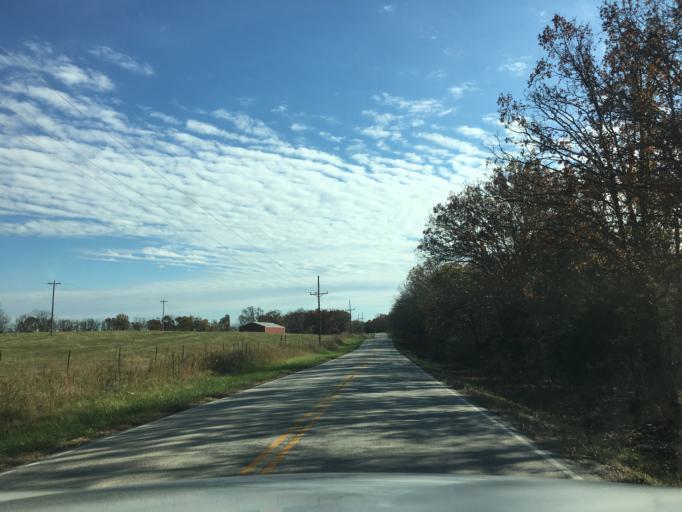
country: US
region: Missouri
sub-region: Maries County
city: Belle
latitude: 38.3621
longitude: -91.8077
